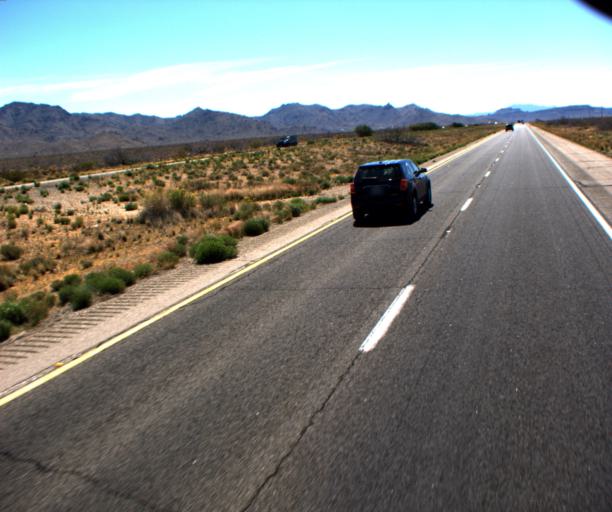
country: US
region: Arizona
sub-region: Mohave County
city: Golden Valley
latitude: 35.2988
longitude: -114.1886
